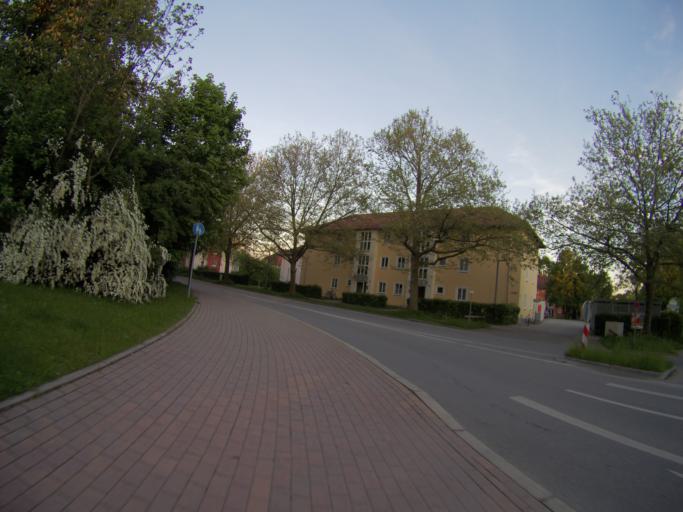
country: DE
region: Bavaria
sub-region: Upper Bavaria
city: Freising
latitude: 48.4087
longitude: 11.7486
